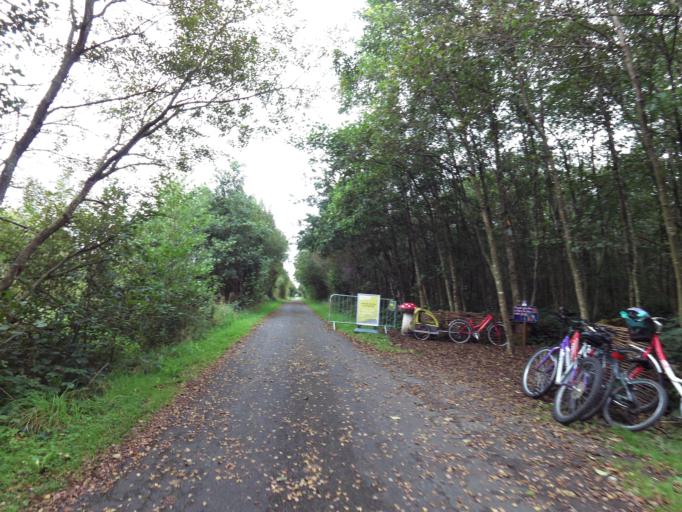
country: IE
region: Leinster
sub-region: Uibh Fhaili
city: Ferbane
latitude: 53.2150
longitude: -7.7317
